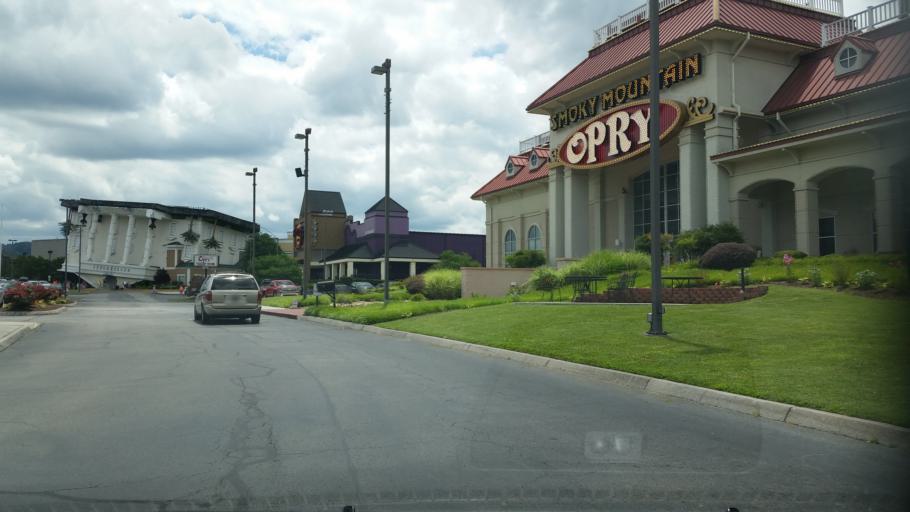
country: US
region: Tennessee
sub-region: Sevier County
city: Pigeon Forge
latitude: 35.8247
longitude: -83.5777
